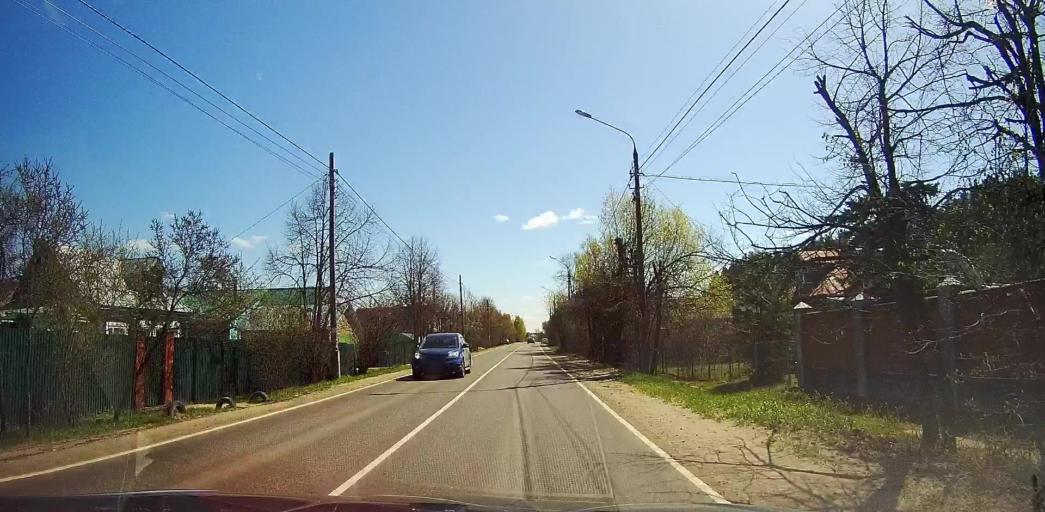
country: RU
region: Moskovskaya
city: Rechitsy
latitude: 55.5372
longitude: 38.4253
